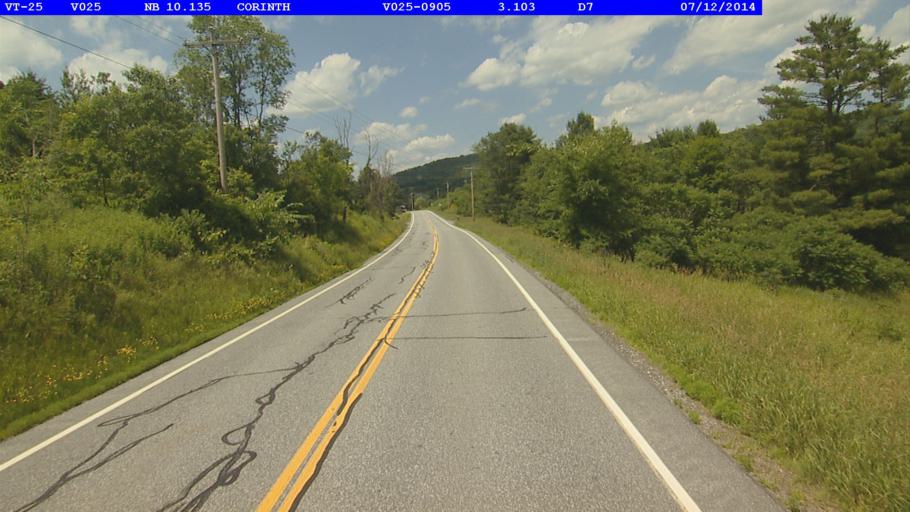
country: US
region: New Hampshire
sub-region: Grafton County
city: Haverhill
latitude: 44.0704
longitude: -72.2478
